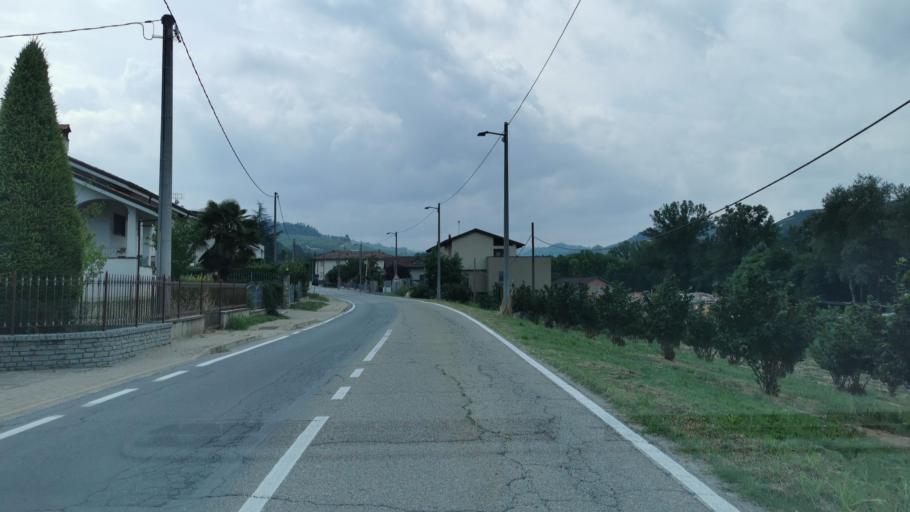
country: IT
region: Piedmont
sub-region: Provincia di Cuneo
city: Grinzane Cavour
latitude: 44.6367
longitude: 8.0053
